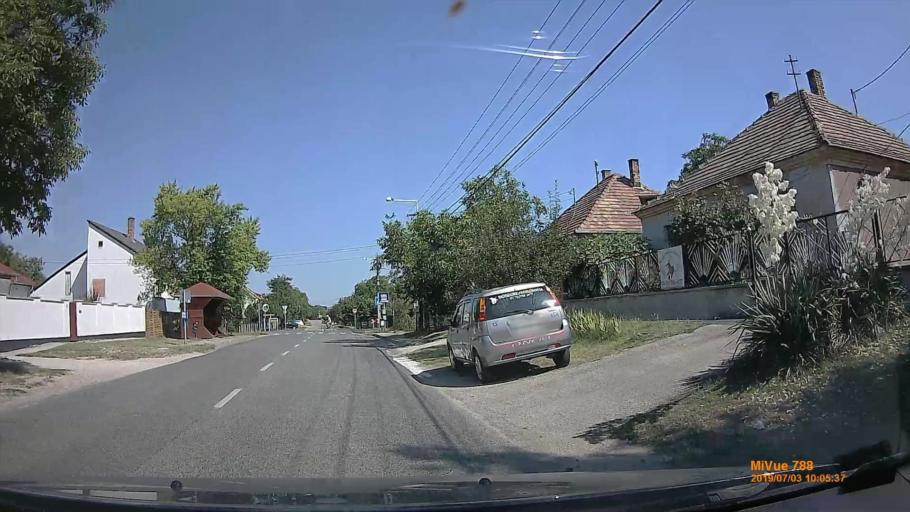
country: HU
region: Gyor-Moson-Sopron
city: Toltestava
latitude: 47.7065
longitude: 17.7262
